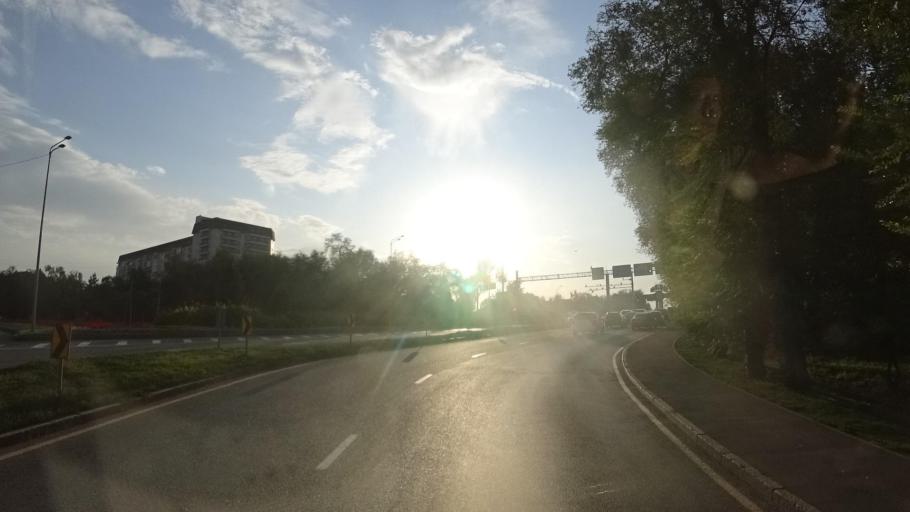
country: KZ
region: Almaty Oblysy
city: Pervomayskiy
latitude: 43.3435
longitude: 76.9964
